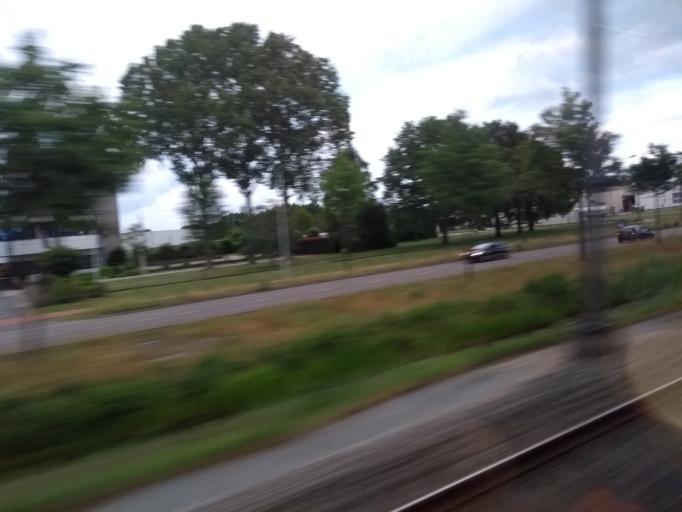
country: NL
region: Friesland
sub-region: Gemeente Heerenveen
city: Oudeschoot
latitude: 52.9311
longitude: 5.9488
